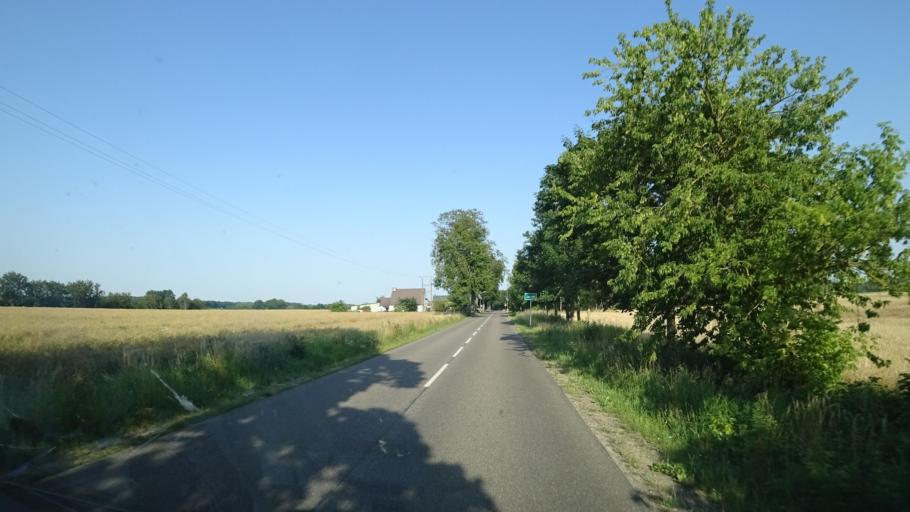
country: PL
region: Pomeranian Voivodeship
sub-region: Powiat czluchowski
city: Przechlewo
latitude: 53.8039
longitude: 17.3039
